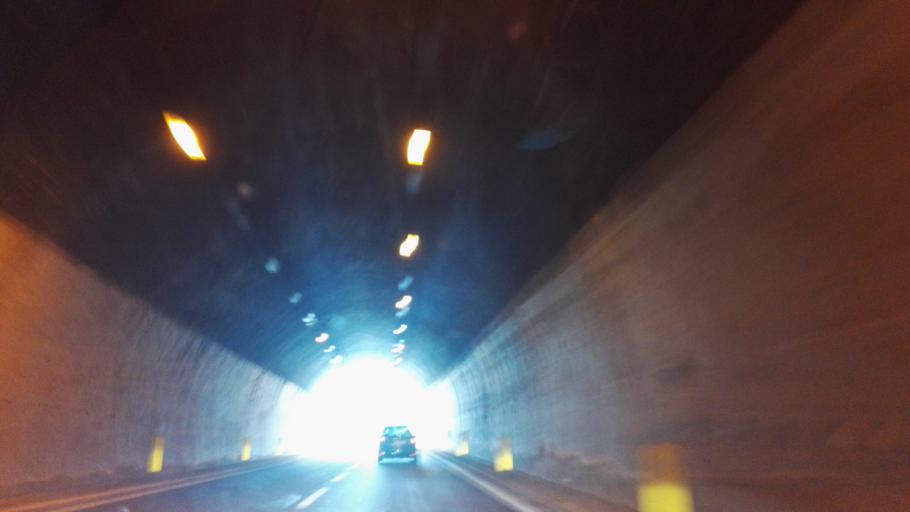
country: IT
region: Calabria
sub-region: Provincia di Cosenza
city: Altilia
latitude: 39.1257
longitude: 16.2620
